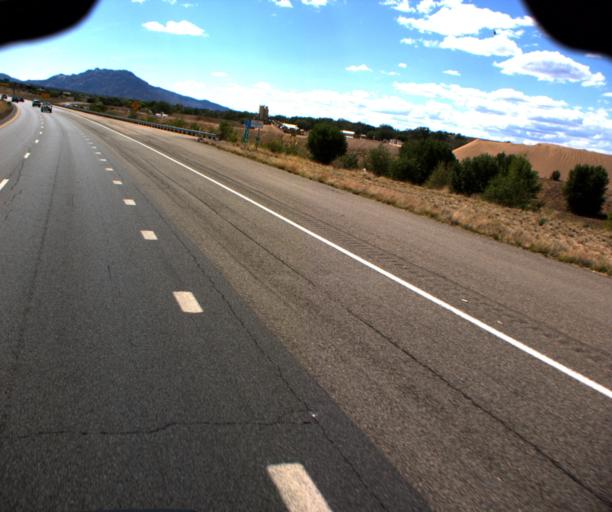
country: US
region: Arizona
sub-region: Yavapai County
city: Prescott Valley
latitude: 34.6374
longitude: -112.4076
